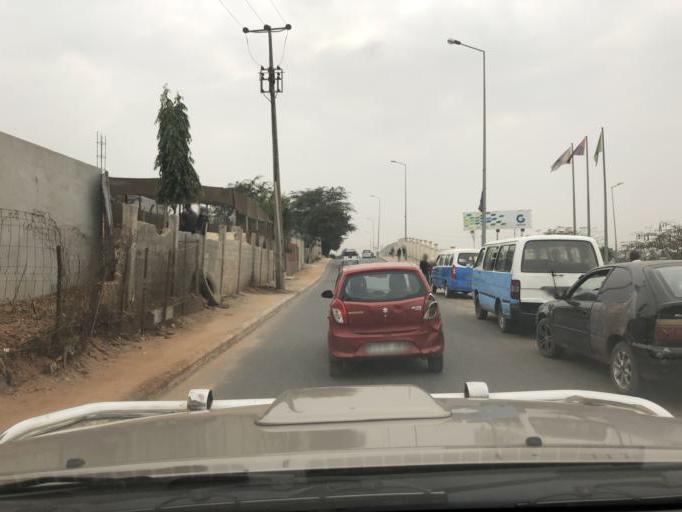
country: AO
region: Luanda
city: Luanda
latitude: -8.8998
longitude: 13.2149
